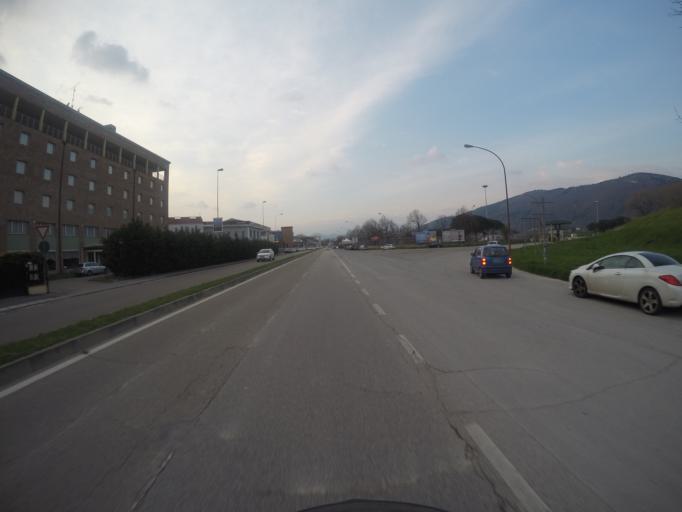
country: IT
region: Tuscany
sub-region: Province of Florence
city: Campi Bisenzio
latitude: 43.8564
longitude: 11.1229
